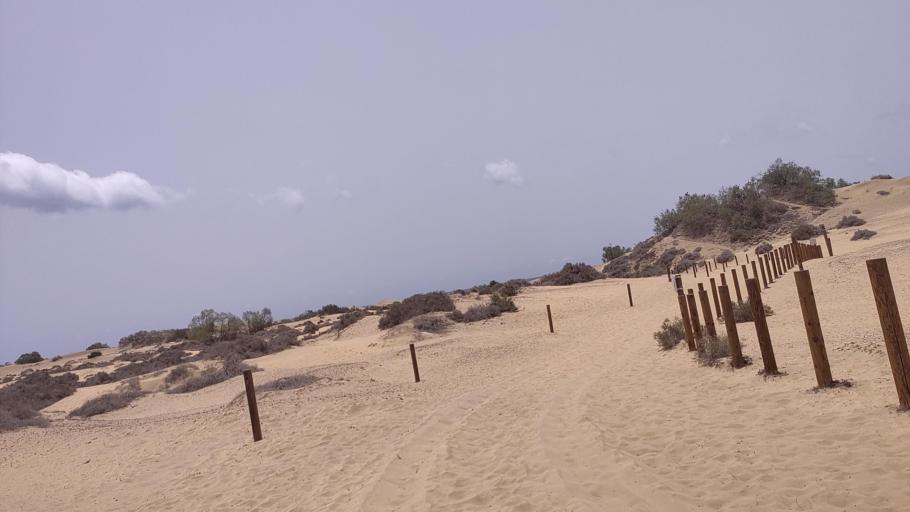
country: ES
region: Canary Islands
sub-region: Provincia de Las Palmas
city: Maspalomas
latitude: 27.7441
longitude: -15.5906
